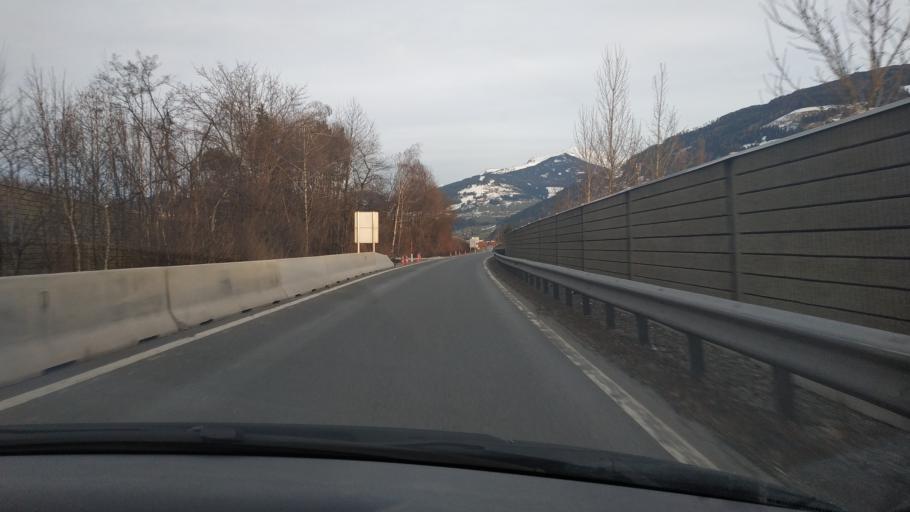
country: AT
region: Tyrol
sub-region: Politischer Bezirk Innsbruck Land
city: Fritzens
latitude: 47.2994
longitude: 11.5815
